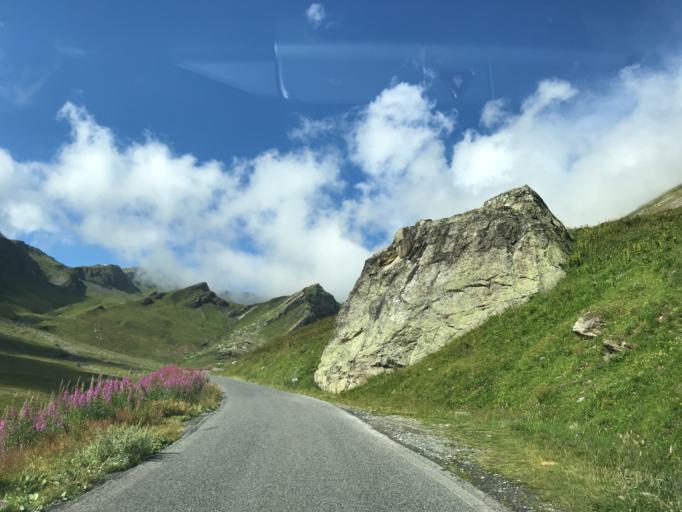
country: IT
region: Piedmont
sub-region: Provincia di Cuneo
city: Pontechianale
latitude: 44.6651
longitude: 6.9868
